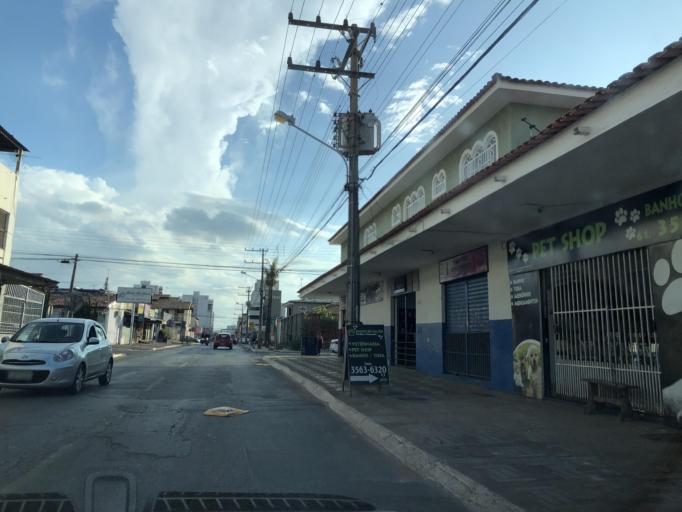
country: BR
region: Federal District
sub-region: Brasilia
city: Brasilia
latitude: -15.8285
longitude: -48.0545
